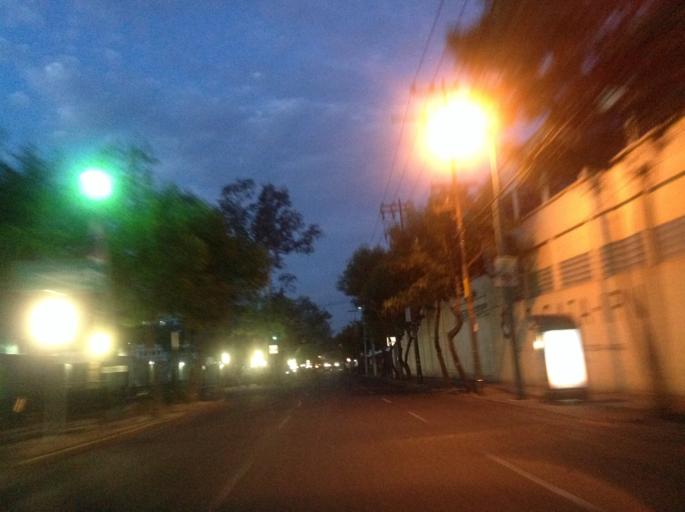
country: MX
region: Mexico City
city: Miguel Hidalgo
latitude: 19.4450
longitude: -99.2100
